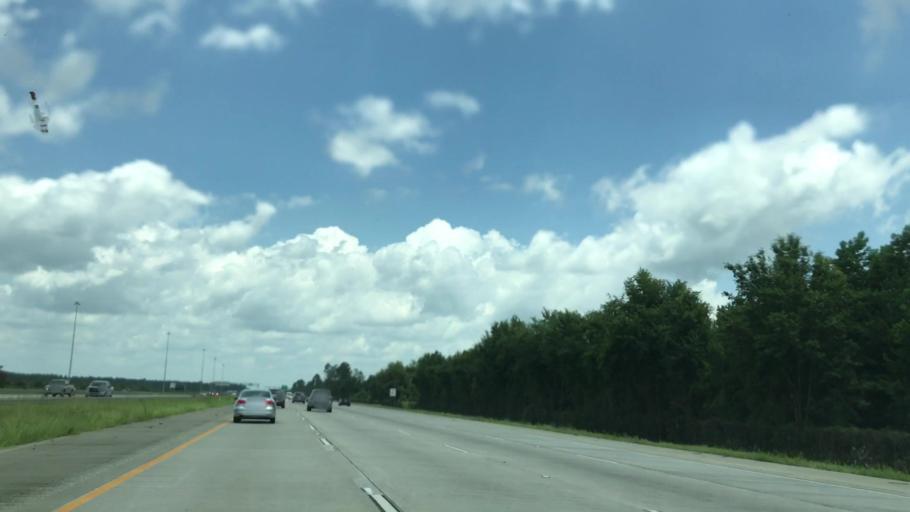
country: US
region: Georgia
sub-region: Glynn County
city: Country Club Estates
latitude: 31.2795
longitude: -81.4885
